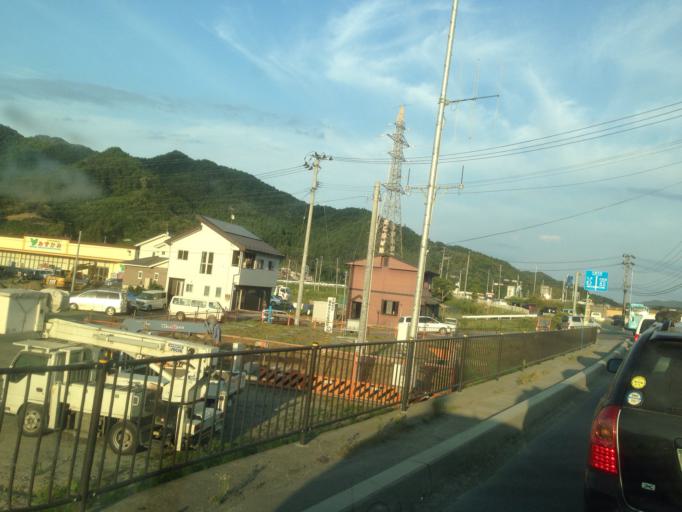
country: JP
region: Iwate
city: Otsuchi
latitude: 39.3652
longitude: 141.9012
